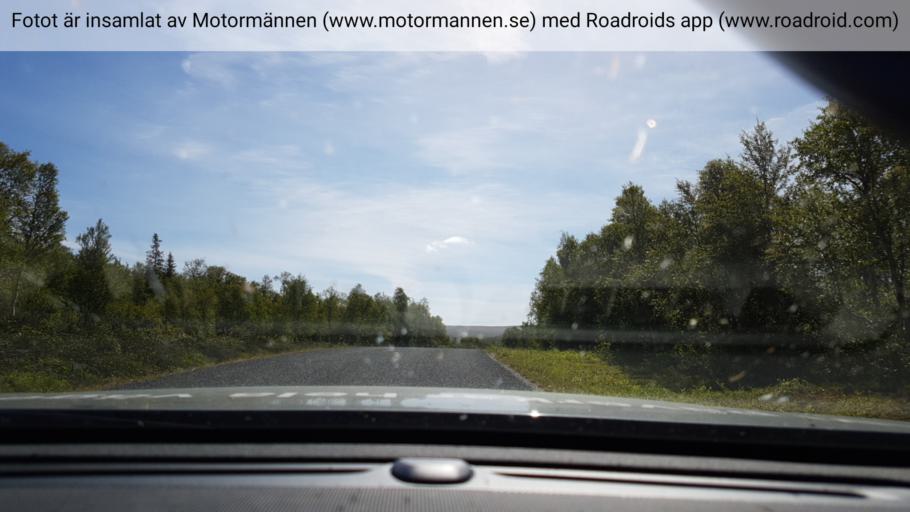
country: NO
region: Nordland
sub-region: Hattfjelldal
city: Hattfjelldal
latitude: 65.4208
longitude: 14.6749
